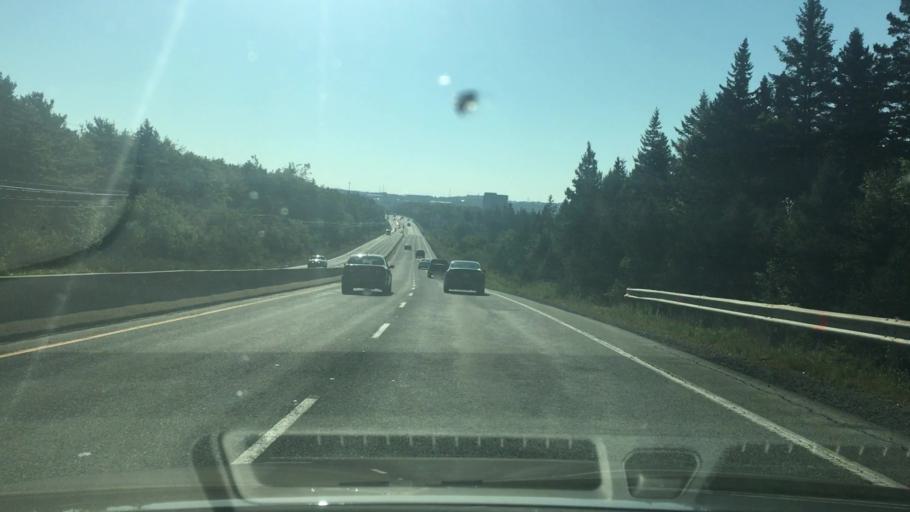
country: CA
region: Nova Scotia
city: Dartmouth
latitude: 44.7085
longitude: -63.6238
